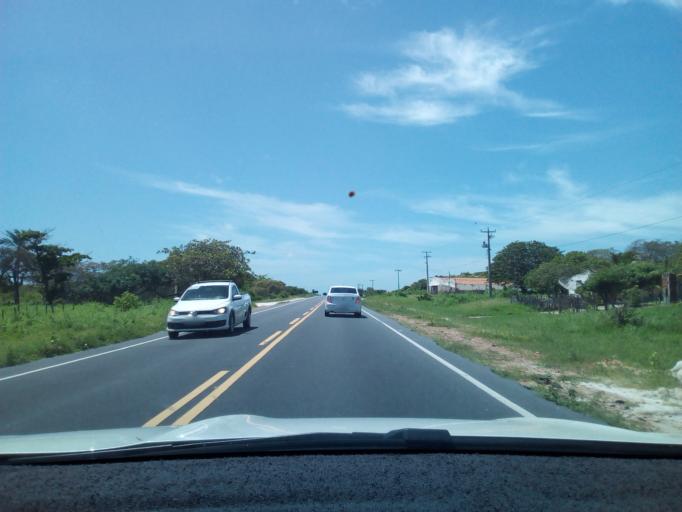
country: BR
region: Ceara
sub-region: Aracati
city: Aracati
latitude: -4.3769
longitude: -37.9188
